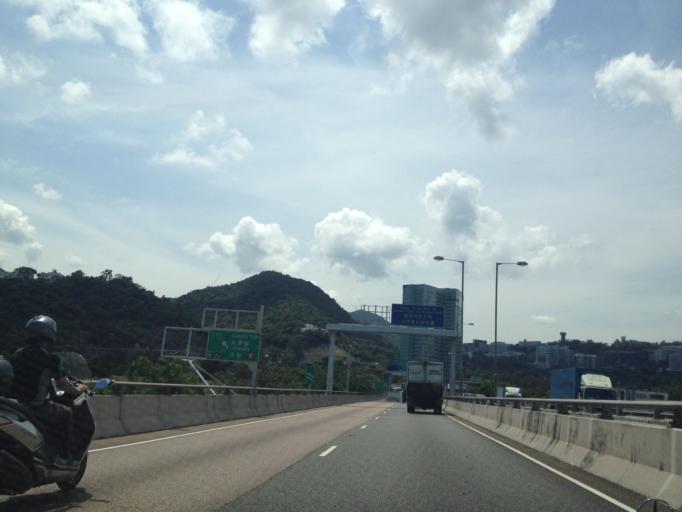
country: HK
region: Sha Tin
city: Sha Tin
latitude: 22.4080
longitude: 114.2155
